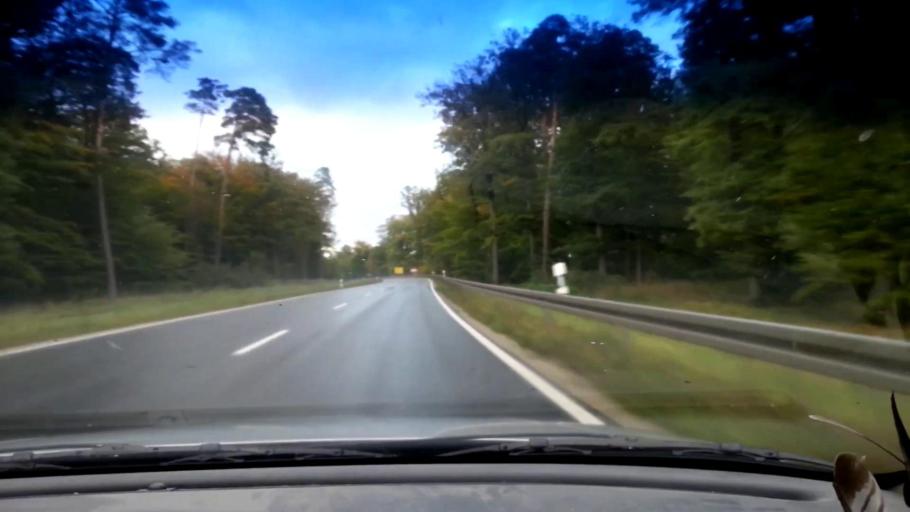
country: DE
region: Bavaria
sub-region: Upper Franconia
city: Burgebrach
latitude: 49.8048
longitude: 10.7288
